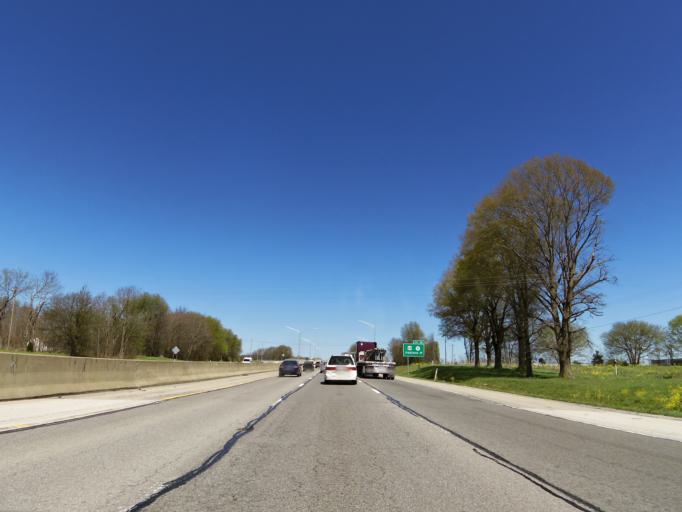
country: US
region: Kentucky
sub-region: Edmonson County
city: Brownsville
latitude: 37.0271
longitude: -86.2445
